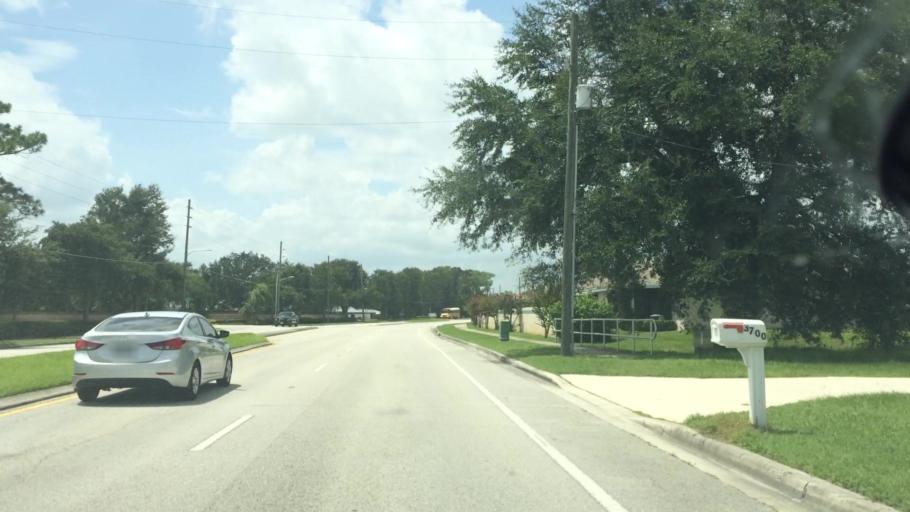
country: US
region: Florida
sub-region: Osceola County
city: Saint Cloud
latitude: 28.2282
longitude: -81.3108
